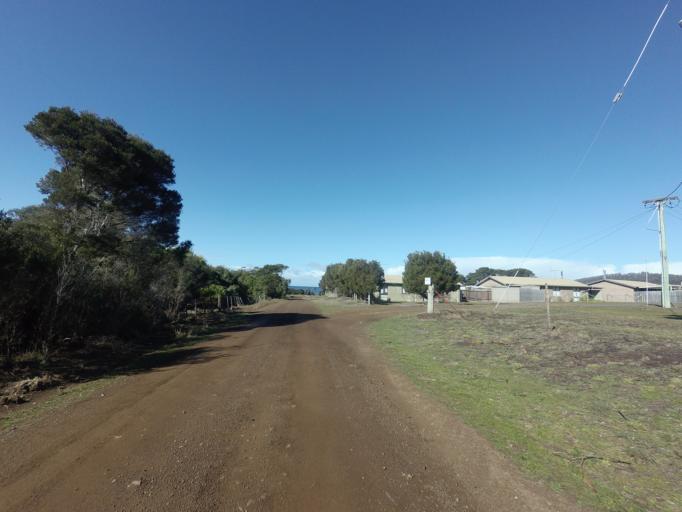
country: AU
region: Tasmania
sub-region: Sorell
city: Sorell
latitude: -42.4021
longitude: 147.9808
